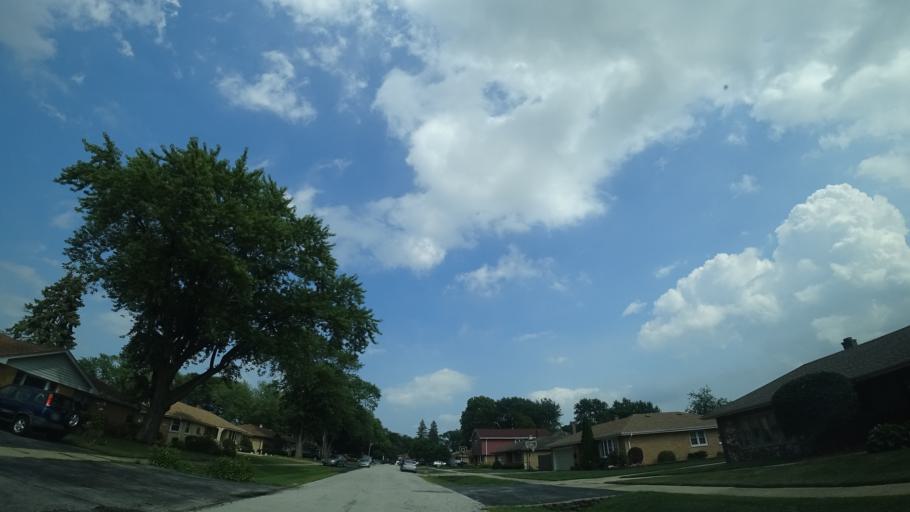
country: US
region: Illinois
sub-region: Cook County
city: Worth
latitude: 41.6818
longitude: -87.7902
